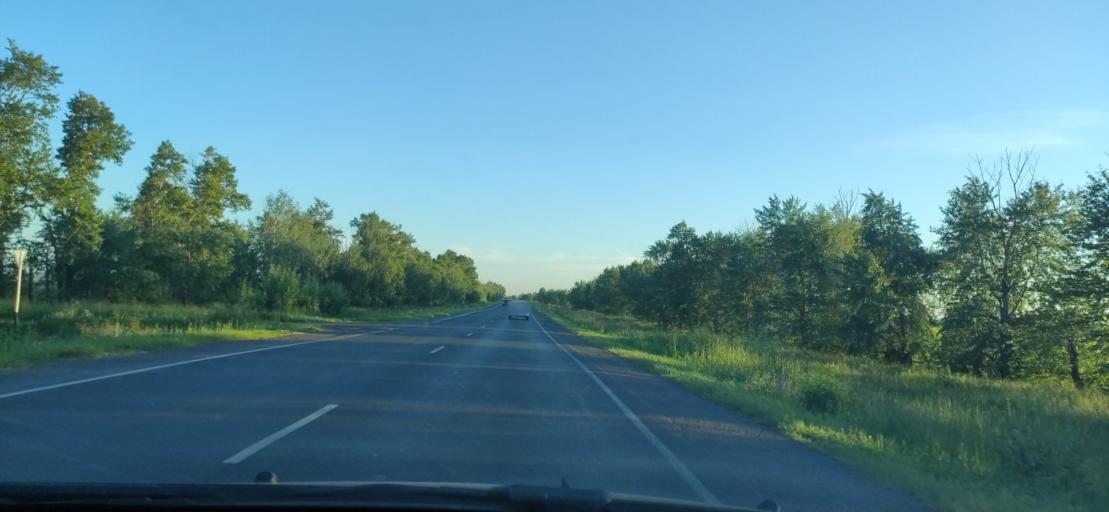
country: RU
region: Ulyanovsk
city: Cherdakly
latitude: 54.4048
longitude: 48.8683
